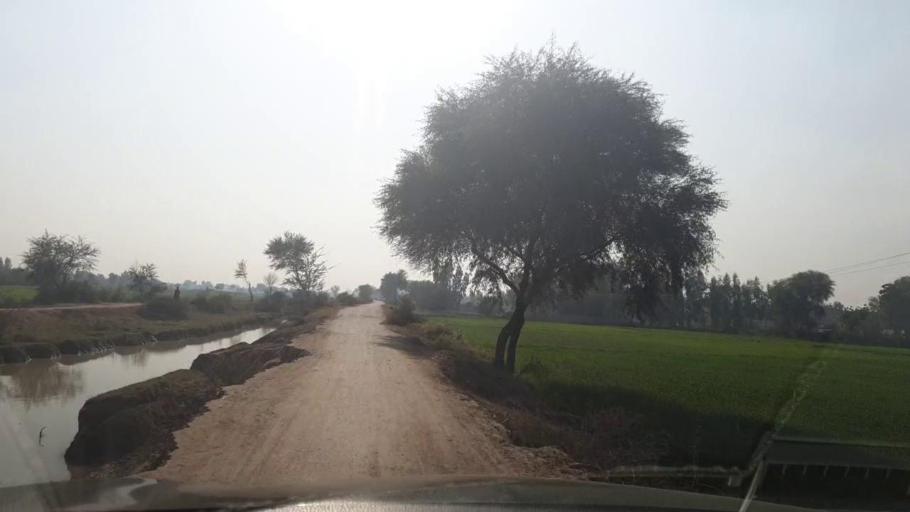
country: PK
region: Sindh
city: Khairpur
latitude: 28.1165
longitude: 69.6406
